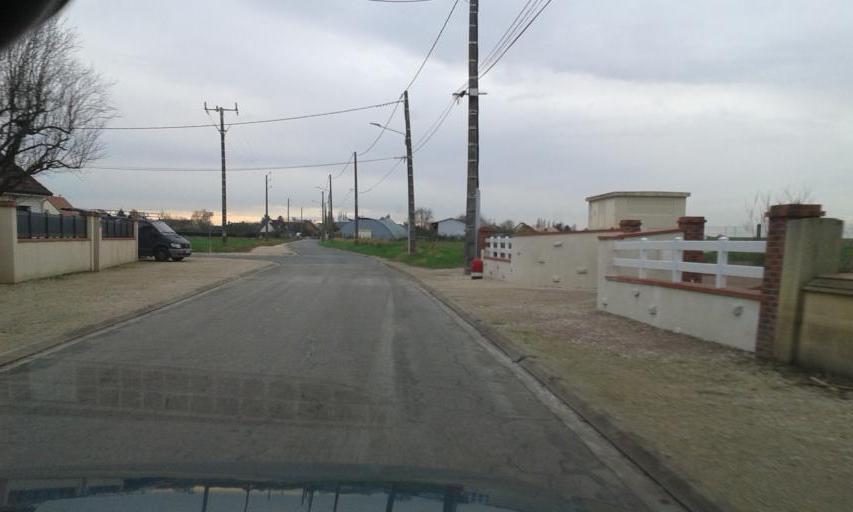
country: FR
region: Centre
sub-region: Departement du Loiret
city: Gidy
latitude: 47.9873
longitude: 1.8361
